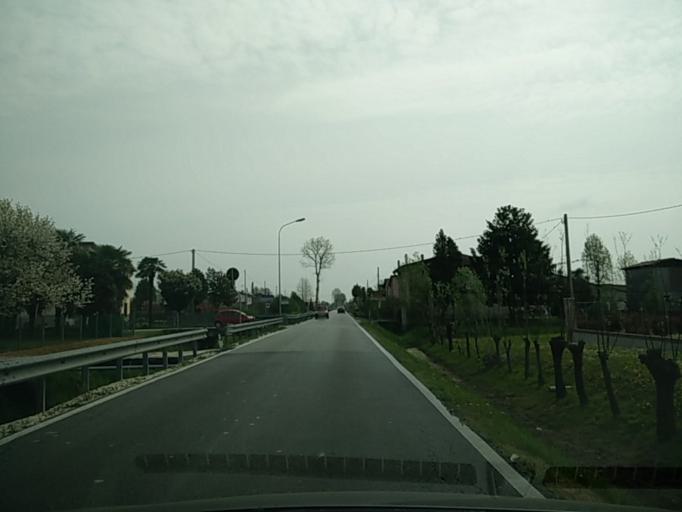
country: IT
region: Veneto
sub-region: Provincia di Venezia
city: Caltana
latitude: 45.4761
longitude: 12.0466
